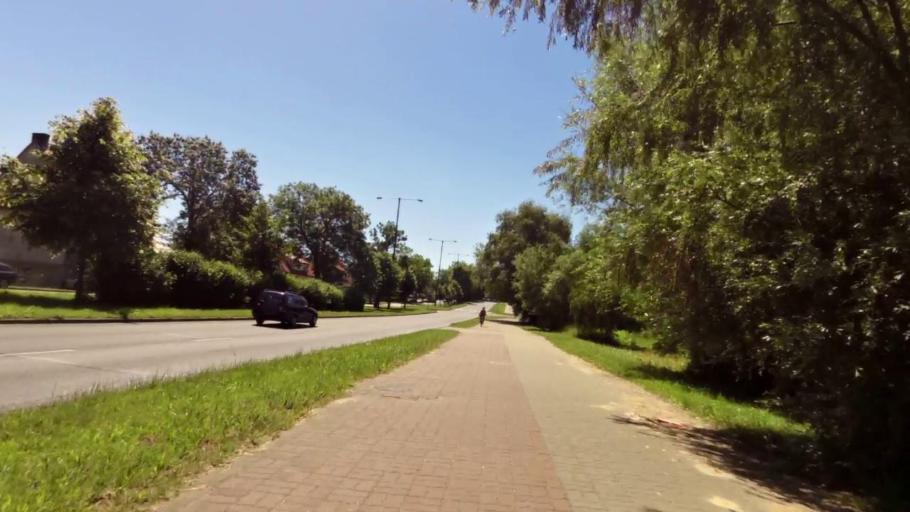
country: PL
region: West Pomeranian Voivodeship
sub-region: Powiat kolobrzeski
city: Kolobrzeg
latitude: 54.1616
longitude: 15.5664
